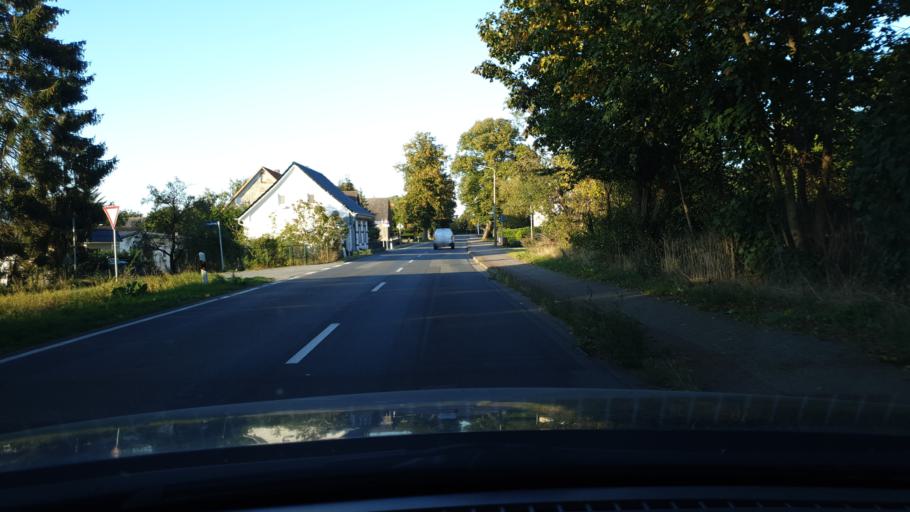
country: DE
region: Mecklenburg-Vorpommern
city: Wittenburg
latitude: 53.5369
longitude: 11.0809
